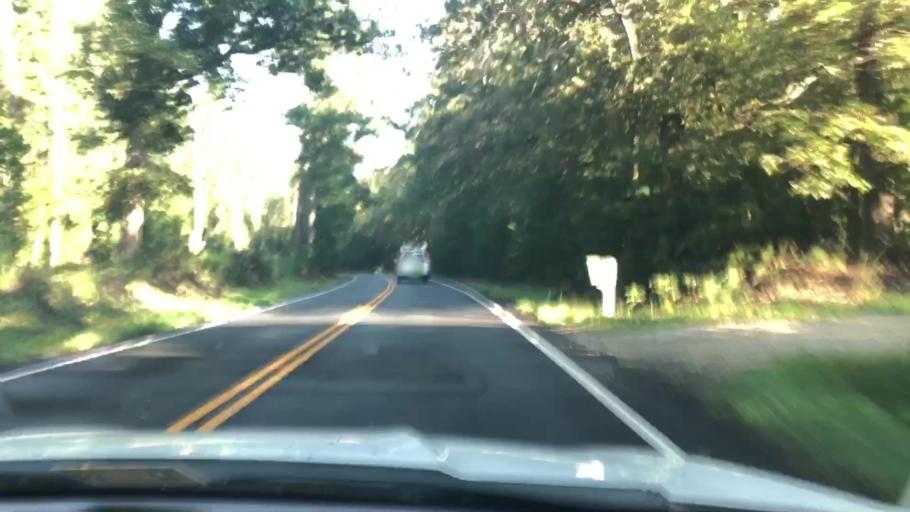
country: US
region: Virginia
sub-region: King William County
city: West Point
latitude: 37.4769
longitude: -76.8466
